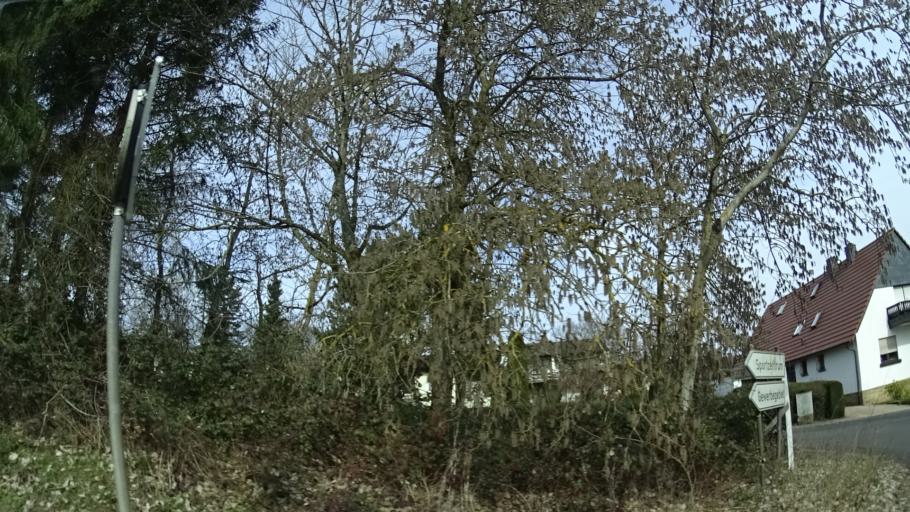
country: DE
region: Rheinland-Pfalz
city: Spabrucken
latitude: 49.9039
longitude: 7.7088
